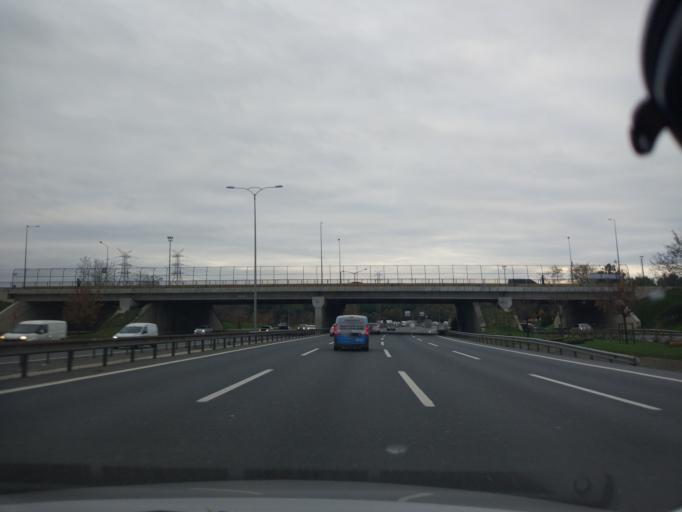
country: TR
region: Istanbul
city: Umraniye
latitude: 41.0895
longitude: 29.0907
